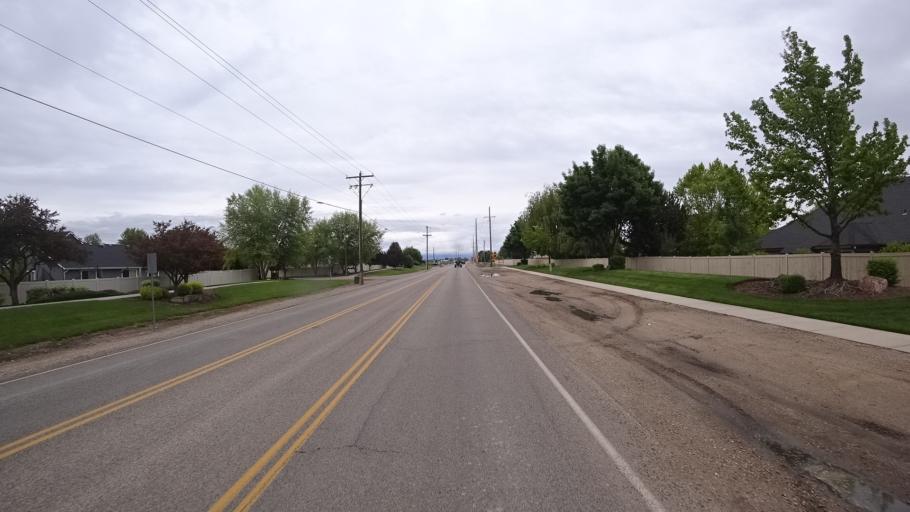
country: US
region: Idaho
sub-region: Ada County
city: Meridian
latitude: 43.6340
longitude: -116.4559
